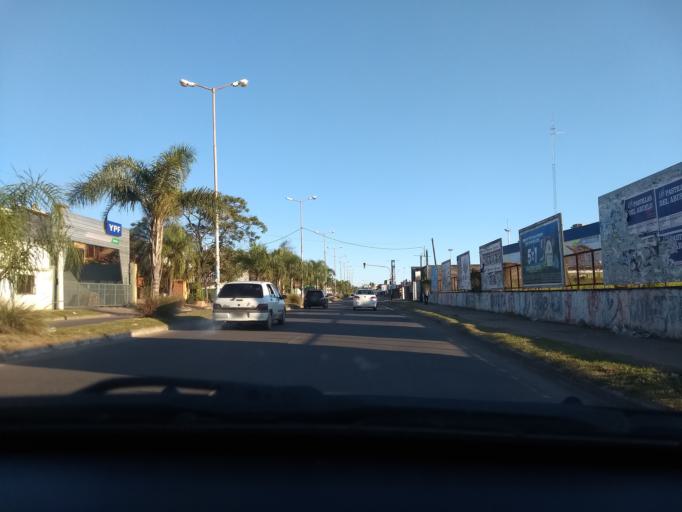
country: AR
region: Corrientes
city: Corrientes
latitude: -27.4759
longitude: -58.8141
